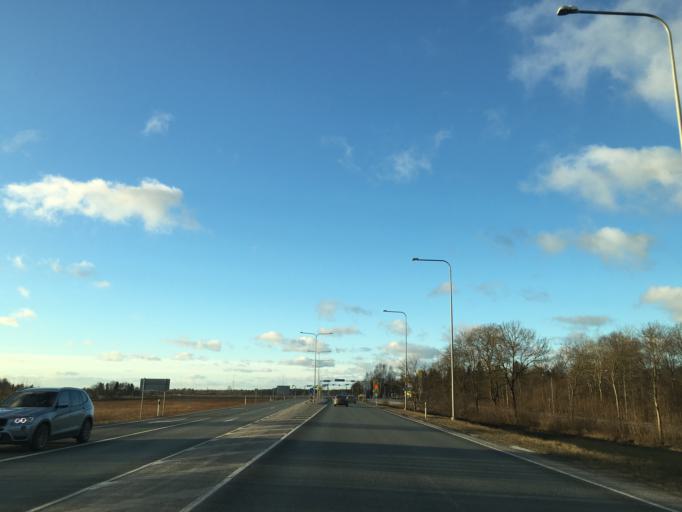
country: EE
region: Harju
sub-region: Saue linn
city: Saue
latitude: 59.3134
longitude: 24.5674
